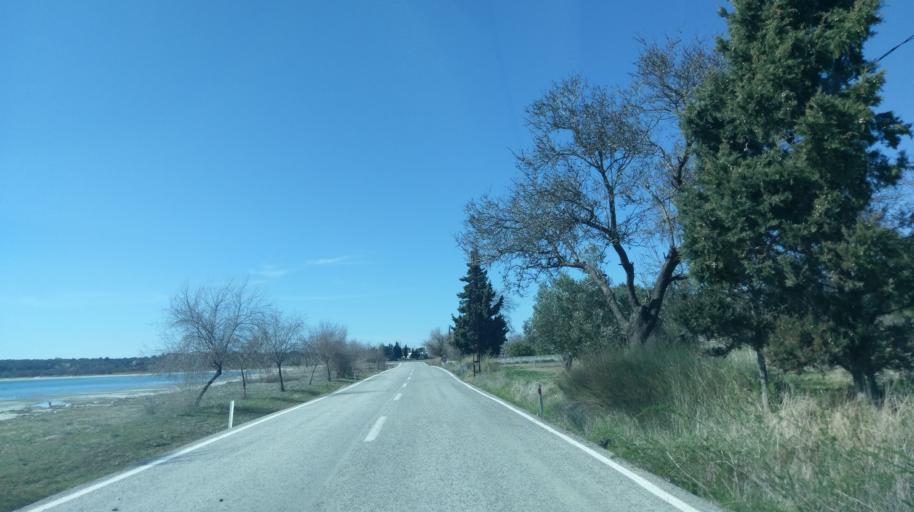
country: TR
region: Canakkale
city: Intepe
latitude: 40.0533
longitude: 26.2114
